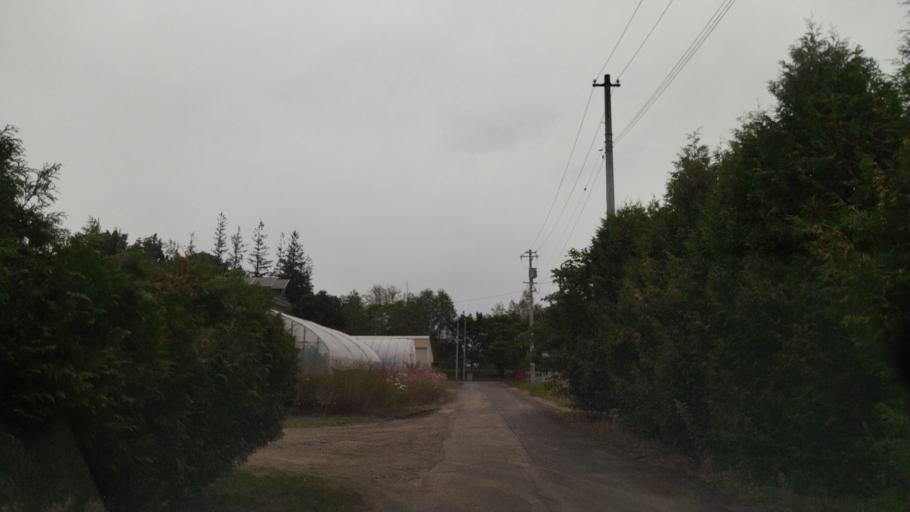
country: JP
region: Hokkaido
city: Otofuke
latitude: 43.2274
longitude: 143.2807
